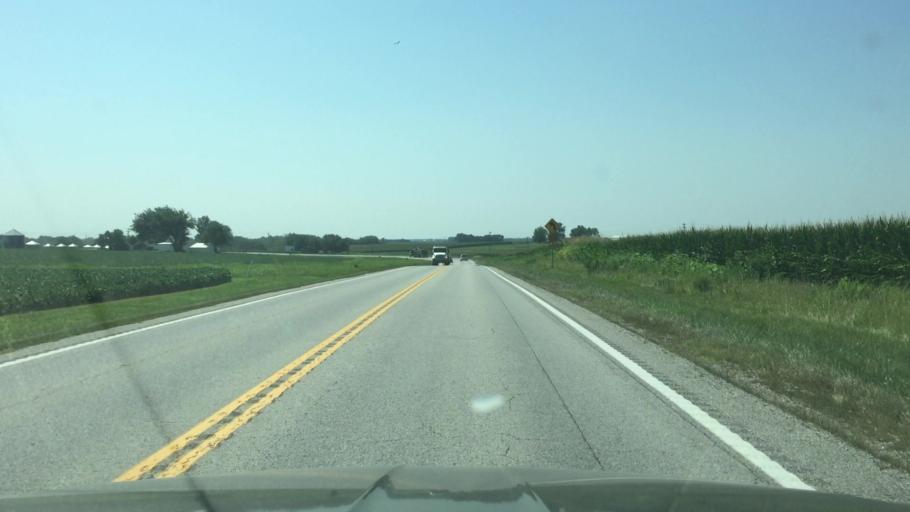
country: US
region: Missouri
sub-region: Moniteau County
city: Tipton
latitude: 38.6575
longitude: -92.8074
